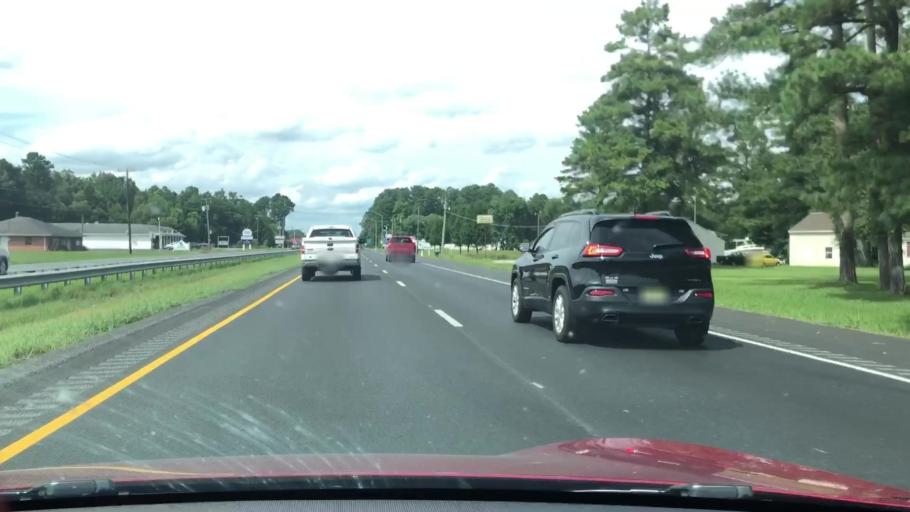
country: US
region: Maryland
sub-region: Worcester County
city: Pocomoke City
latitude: 38.0377
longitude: -75.5420
